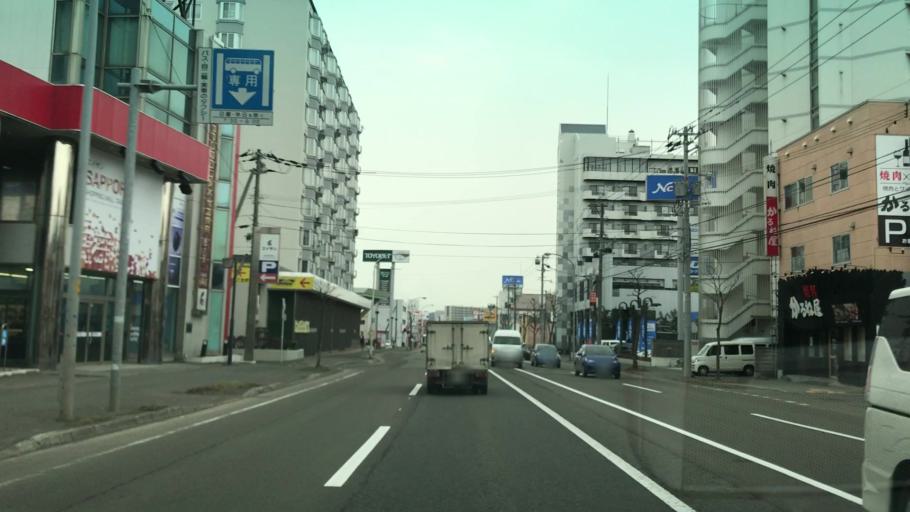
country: JP
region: Hokkaido
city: Sapporo
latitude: 43.0704
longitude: 141.3040
